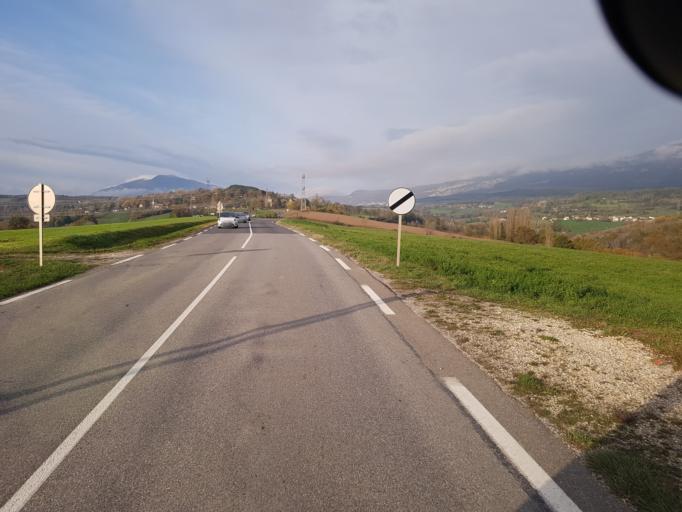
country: FR
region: Rhone-Alpes
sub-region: Departement de la Haute-Savoie
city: Frangy
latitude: 46.0331
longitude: 5.8881
